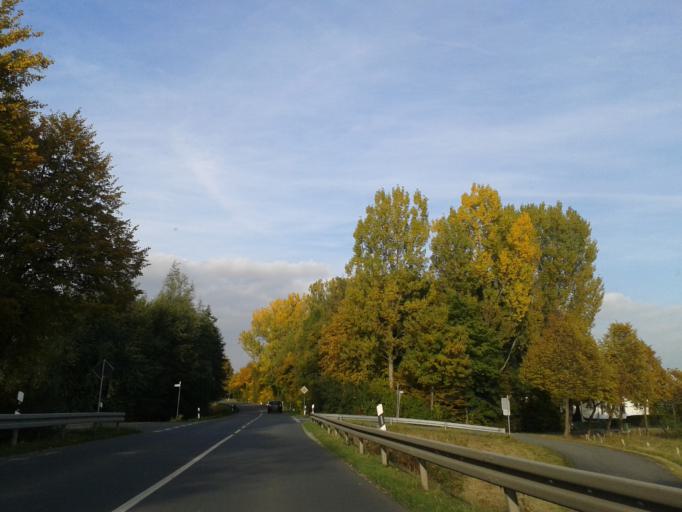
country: DE
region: North Rhine-Westphalia
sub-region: Regierungsbezirk Detmold
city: Salzkotten
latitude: 51.7244
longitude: 8.6617
